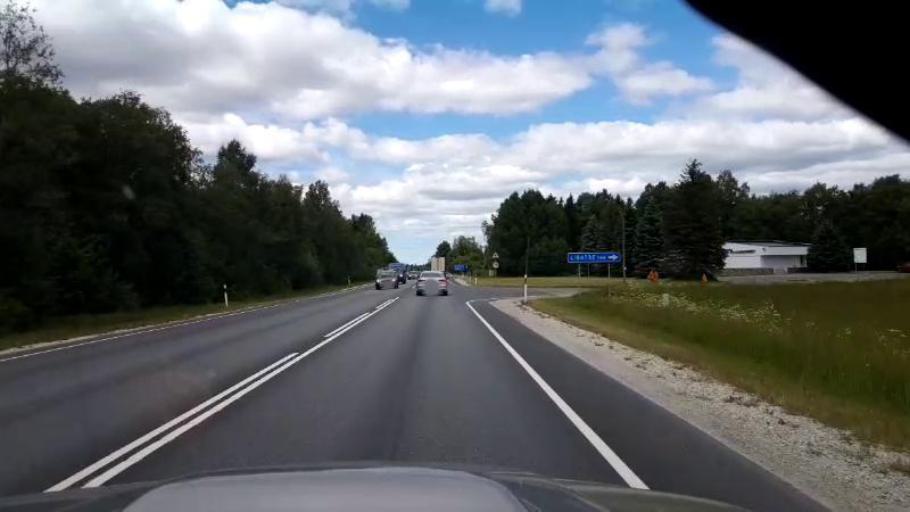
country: EE
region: Paernumaa
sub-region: Halinga vald
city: Parnu-Jaagupi
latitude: 58.6574
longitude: 24.4727
